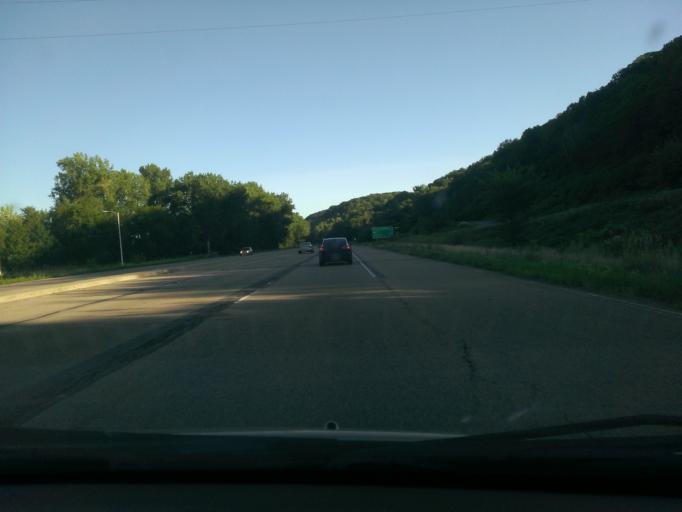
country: US
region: Minnesota
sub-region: Nicollet County
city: North Mankato
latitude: 44.2209
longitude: -94.0276
